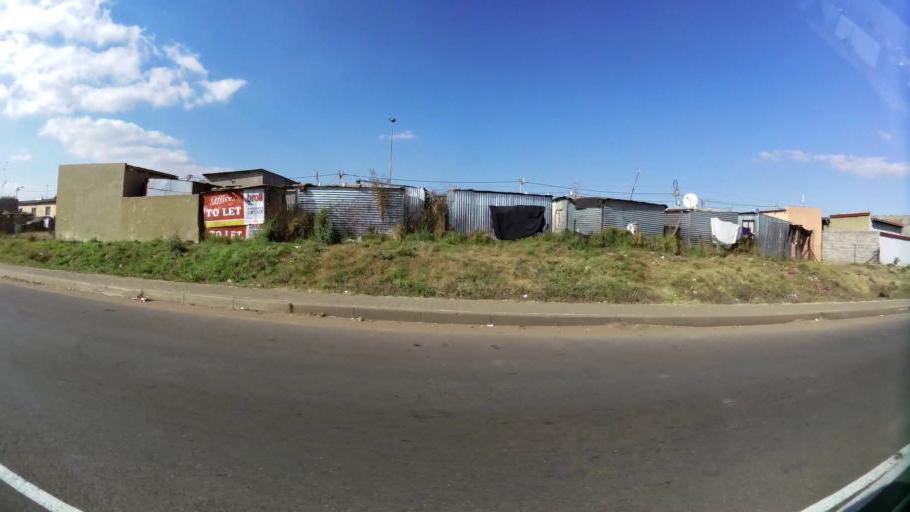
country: ZA
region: Gauteng
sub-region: City of Johannesburg Metropolitan Municipality
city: Soweto
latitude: -26.2719
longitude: 27.8906
